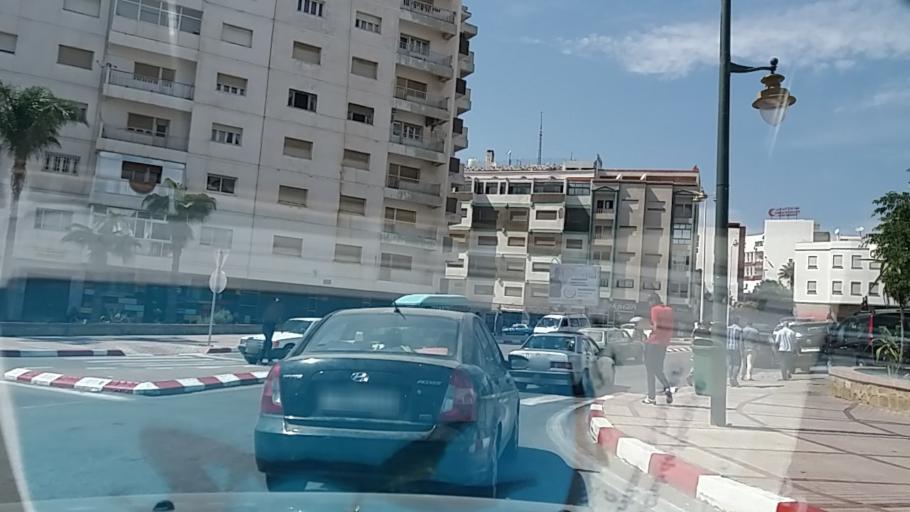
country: MA
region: Tanger-Tetouan
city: Tetouan
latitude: 35.5703
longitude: -5.3858
